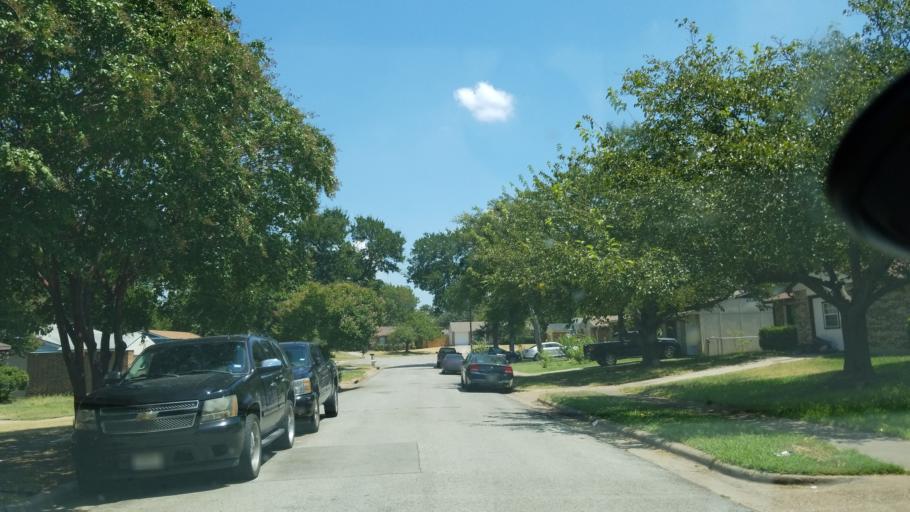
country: US
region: Texas
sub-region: Dallas County
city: Duncanville
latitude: 32.6689
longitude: -96.8931
